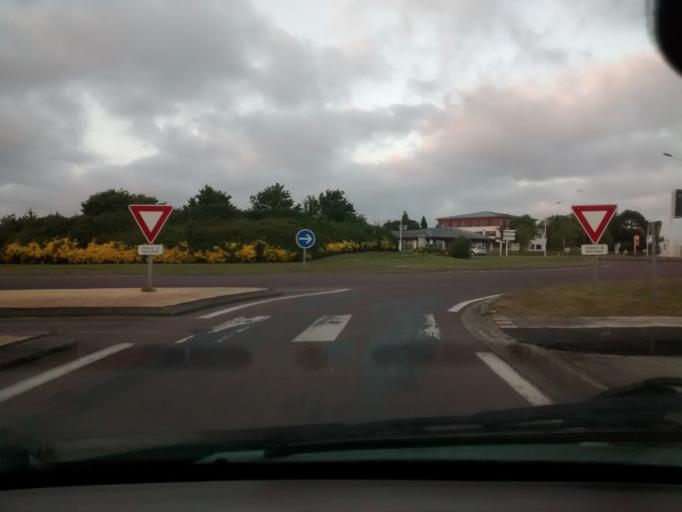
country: FR
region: Lower Normandy
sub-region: Departement de la Manche
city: Saint-Lo
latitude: 49.0997
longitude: -1.0819
